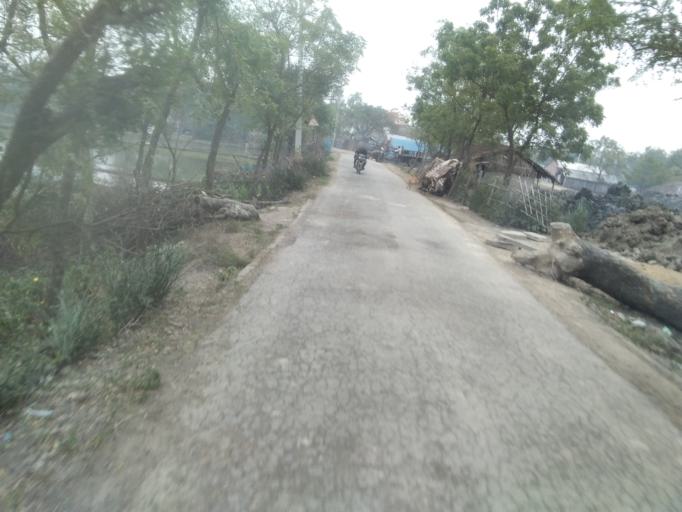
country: BD
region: Khulna
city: Satkhira
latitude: 22.5734
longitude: 89.0770
